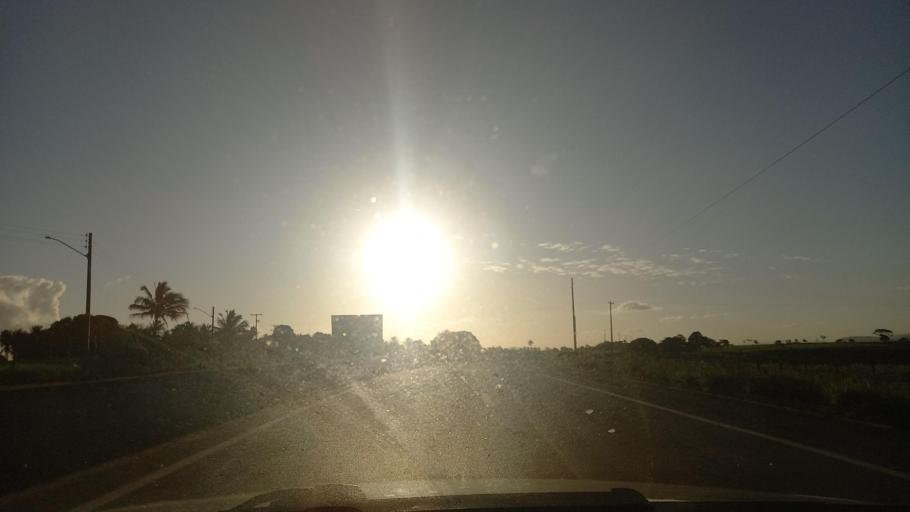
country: BR
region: Alagoas
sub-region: Limoeiro De Anadia
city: Limoeiro de Anadia
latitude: -9.7615
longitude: -36.5110
